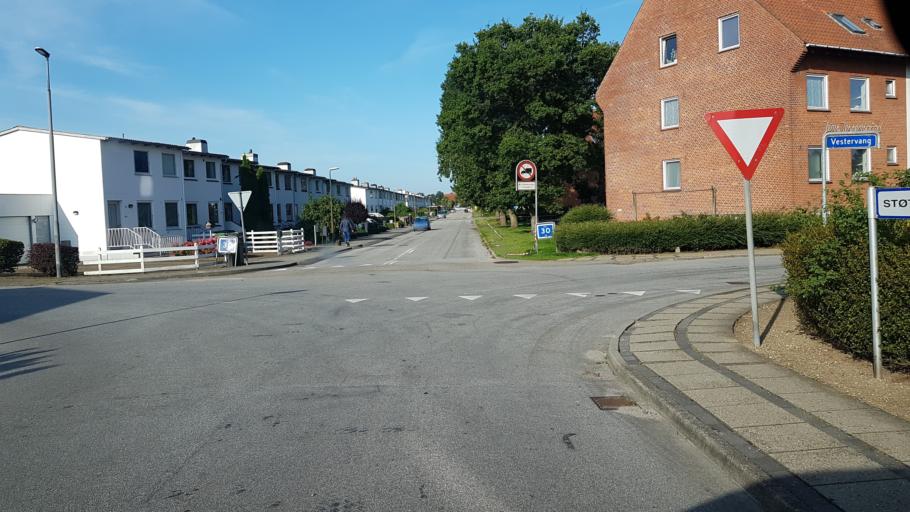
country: DK
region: South Denmark
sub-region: Haderslev Kommune
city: Vojens
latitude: 55.2447
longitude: 9.3031
